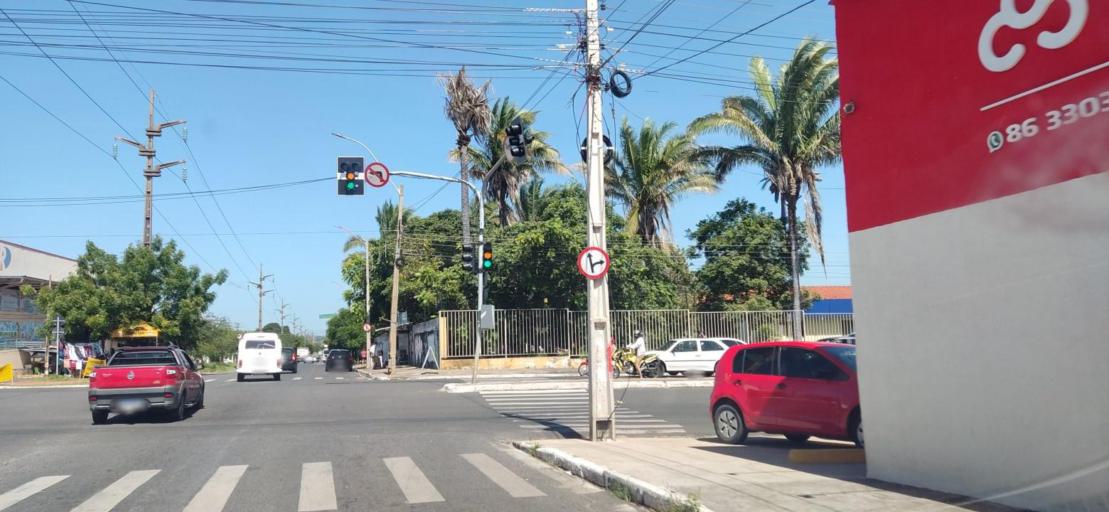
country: BR
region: Piaui
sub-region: Teresina
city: Teresina
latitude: -5.1193
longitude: -42.8027
